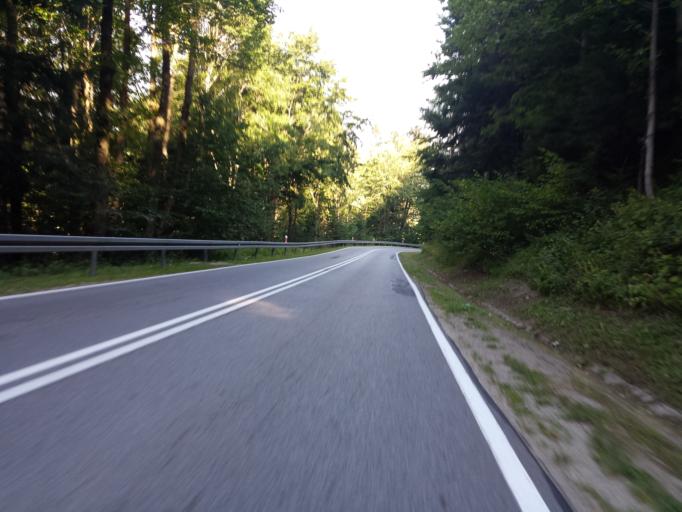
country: PL
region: Subcarpathian Voivodeship
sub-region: Powiat leski
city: Cisna
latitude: 49.2484
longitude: 22.2890
